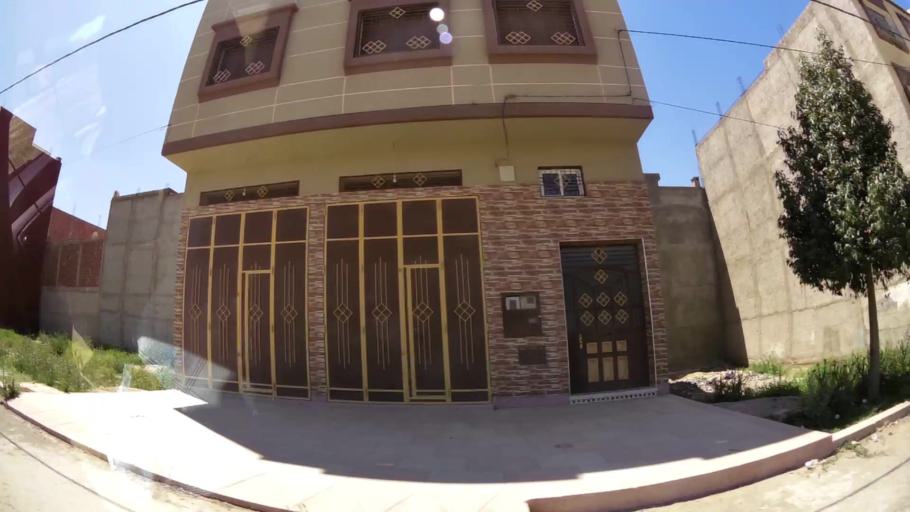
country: MA
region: Oriental
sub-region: Oujda-Angad
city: Oujda
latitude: 34.6849
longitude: -1.9462
